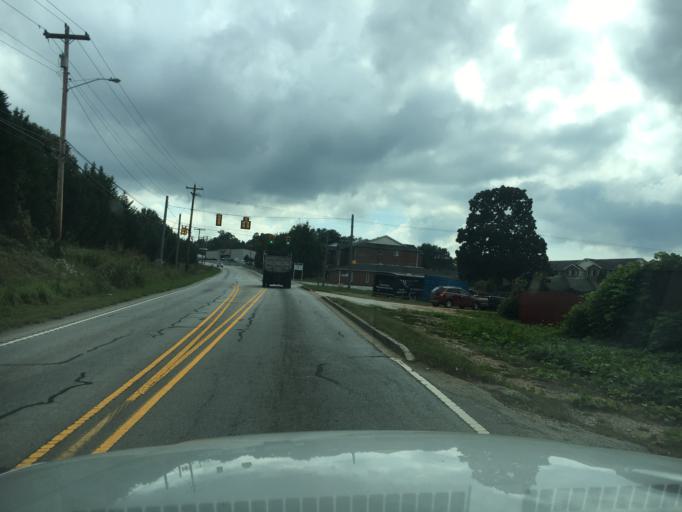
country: US
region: South Carolina
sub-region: Greenville County
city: Greer
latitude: 34.9564
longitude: -82.2298
